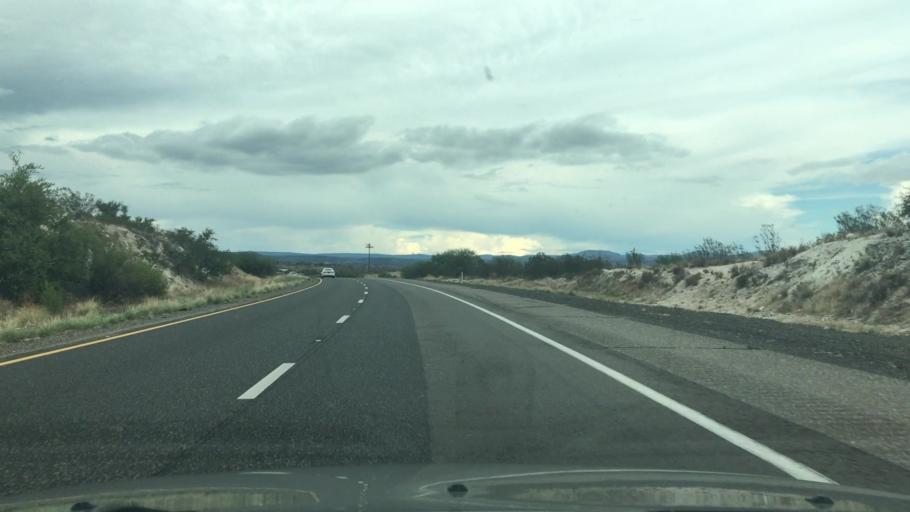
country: US
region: Arizona
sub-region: Yavapai County
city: Lake Montezuma
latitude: 34.6259
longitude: -111.8372
